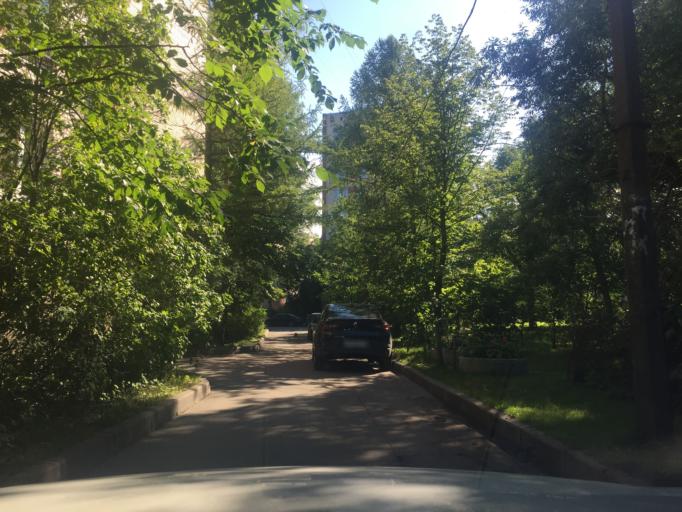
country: RU
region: St.-Petersburg
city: Pushkin
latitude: 59.7342
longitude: 30.4152
